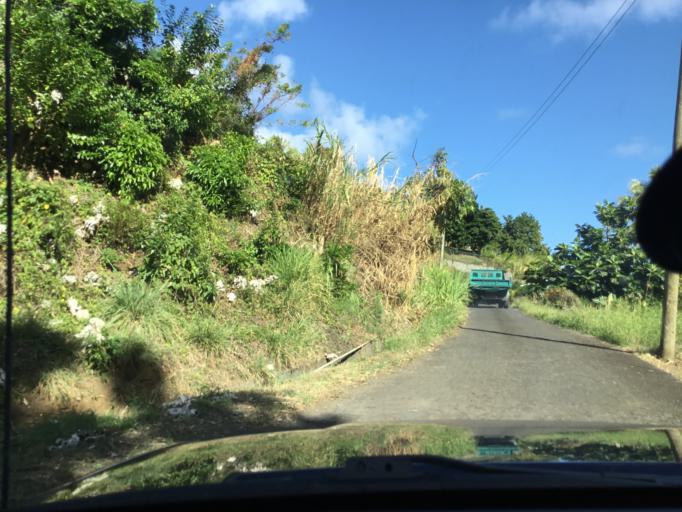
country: VC
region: Charlotte
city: Biabou
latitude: 13.1605
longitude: -61.1692
